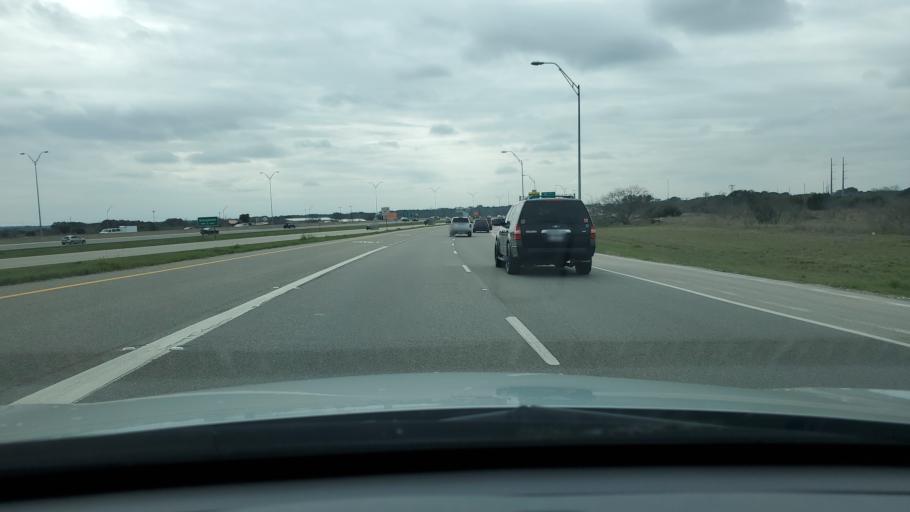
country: US
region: Texas
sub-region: Williamson County
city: Serenada
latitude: 30.7008
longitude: -97.6532
